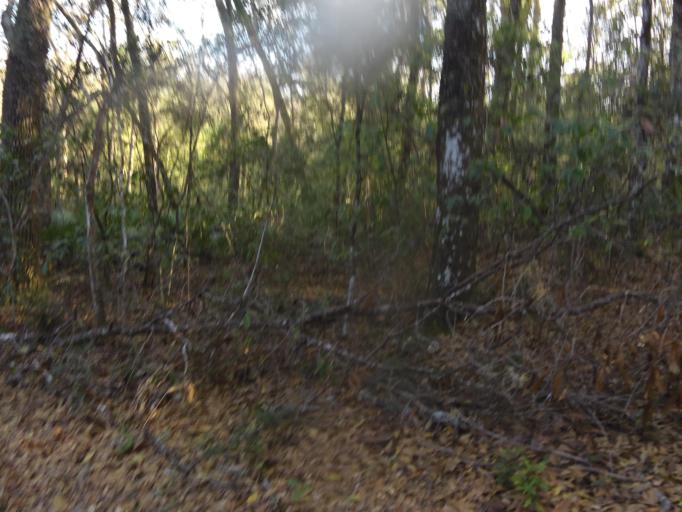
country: US
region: Florida
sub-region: Clay County
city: Middleburg
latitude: 30.1464
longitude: -81.9500
